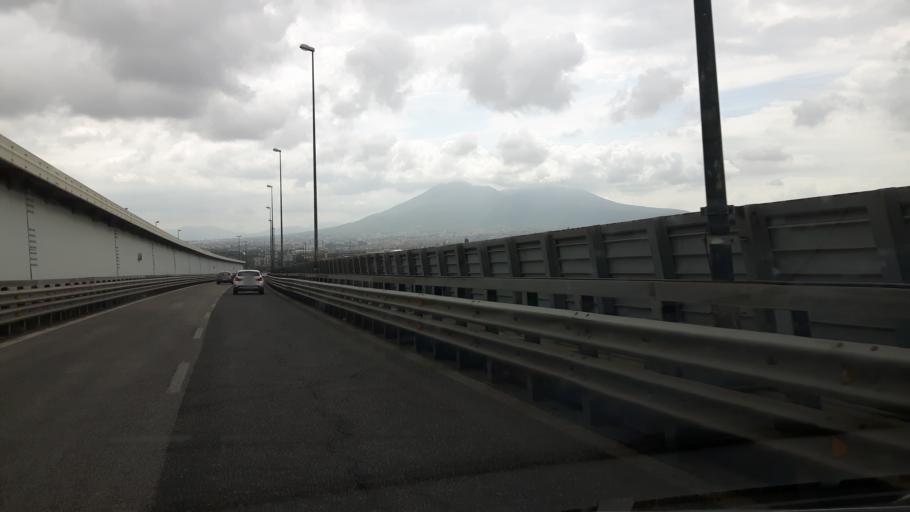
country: IT
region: Campania
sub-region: Provincia di Napoli
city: Casavatore
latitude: 40.8634
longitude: 14.2823
